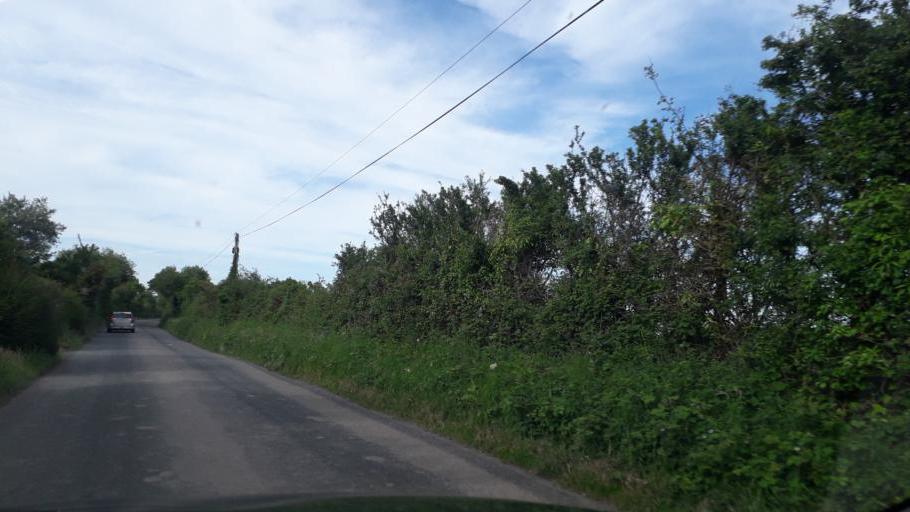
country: IE
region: Leinster
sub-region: Loch Garman
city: Courtown
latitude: 52.5258
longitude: -6.2701
